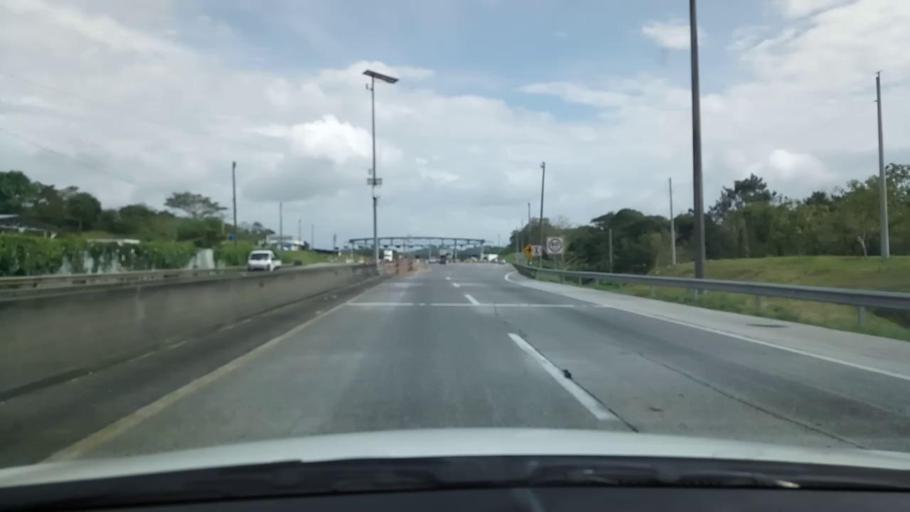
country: PA
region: Colon
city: Buena Vista
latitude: 9.2643
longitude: -79.7026
